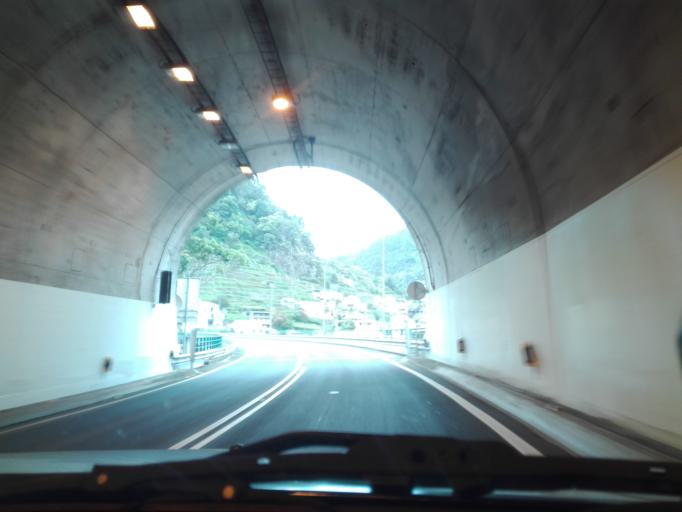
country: PT
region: Madeira
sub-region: Machico
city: Machico
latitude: 32.7329
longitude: -16.7890
